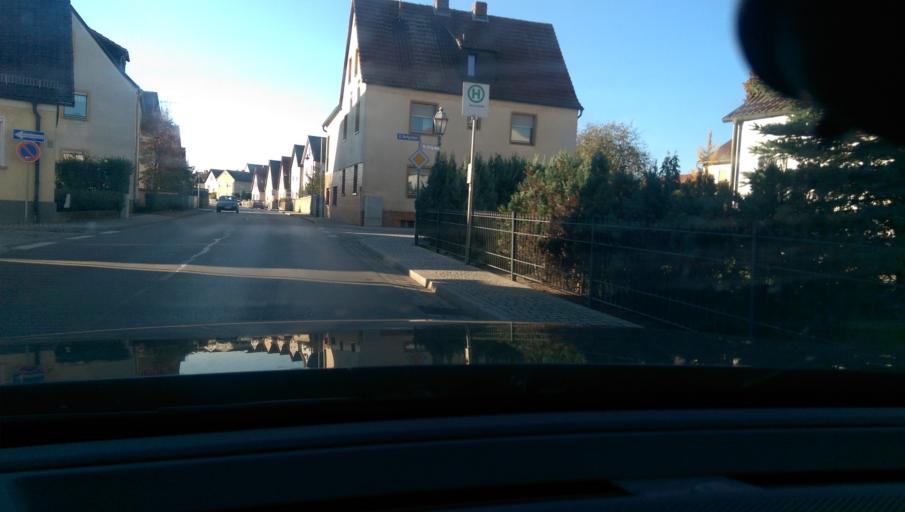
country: DE
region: Bavaria
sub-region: Regierungsbezirk Unterfranken
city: Grafenrheinfeld
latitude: 50.0039
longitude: 10.1967
